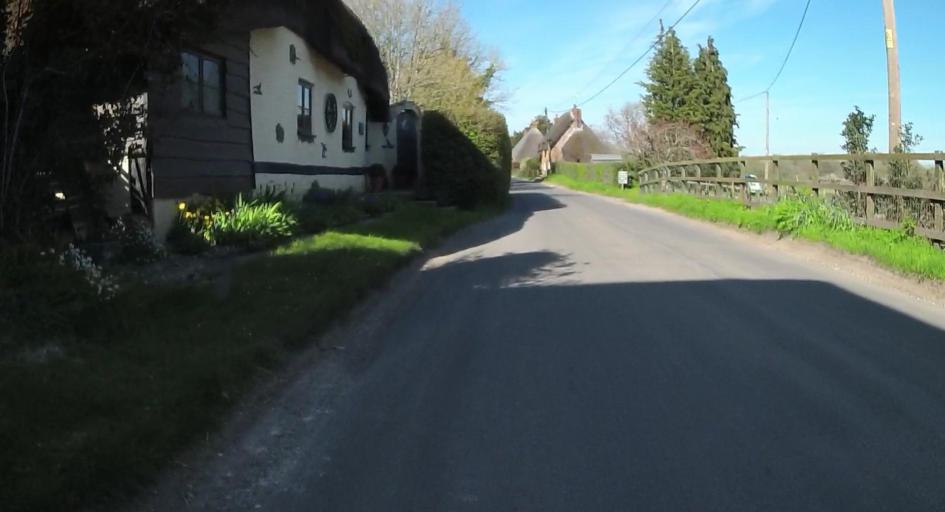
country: GB
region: England
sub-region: Hampshire
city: Abbotts Ann
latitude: 51.1344
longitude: -1.4859
